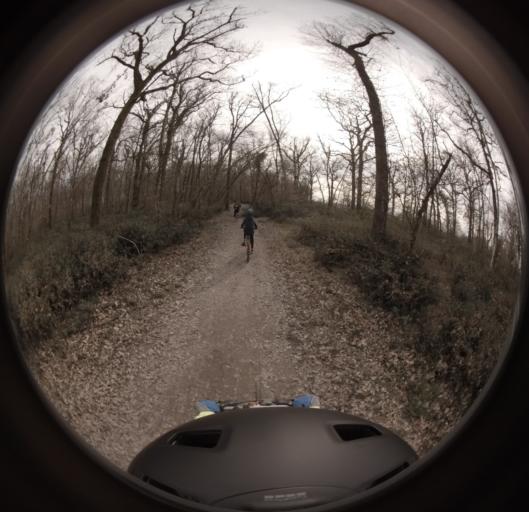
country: FR
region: Midi-Pyrenees
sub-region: Departement du Tarn-et-Garonne
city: Montech
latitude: 43.9607
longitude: 1.2595
